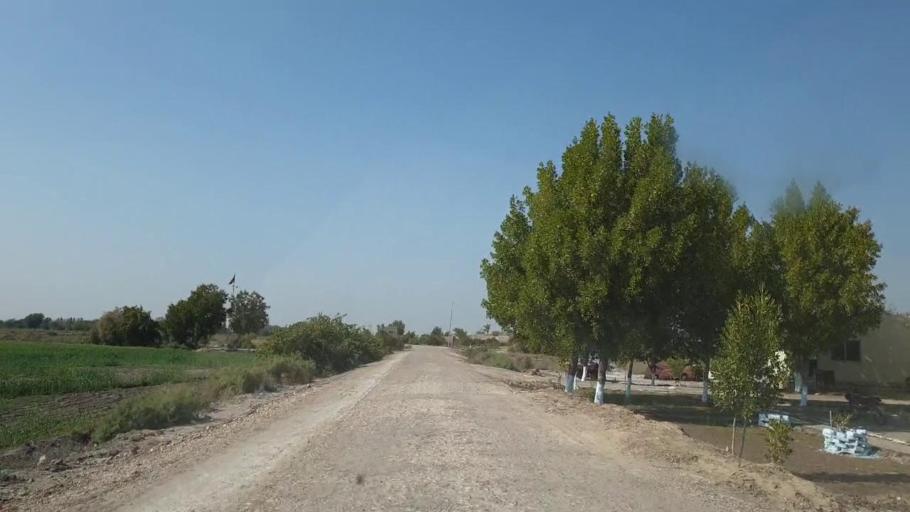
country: PK
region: Sindh
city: Mirpur Khas
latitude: 25.7150
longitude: 69.1326
